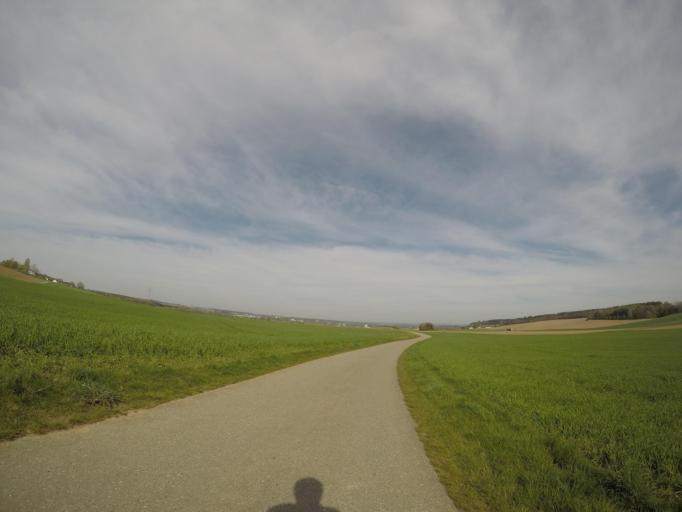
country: DE
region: Baden-Wuerttemberg
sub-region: Tuebingen Region
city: Allmannsweiler
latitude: 48.0060
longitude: 9.5532
